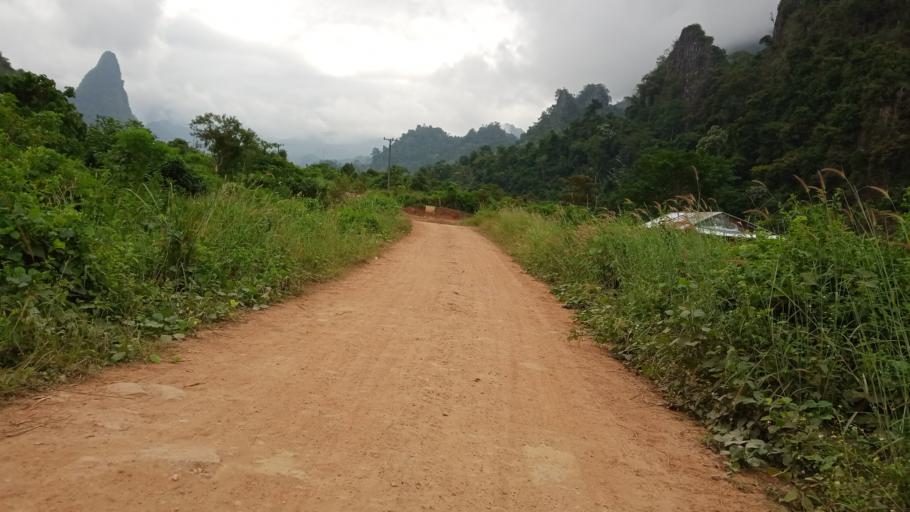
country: LA
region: Xiangkhoang
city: Phonsavan
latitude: 19.0879
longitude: 103.0071
